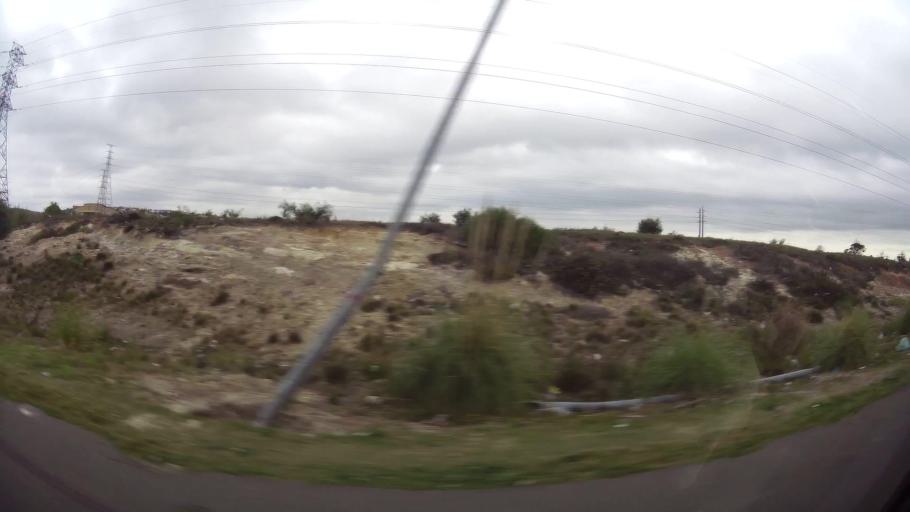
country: ZA
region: Eastern Cape
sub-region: Nelson Mandela Bay Metropolitan Municipality
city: Port Elizabeth
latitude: -33.9198
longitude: 25.5688
